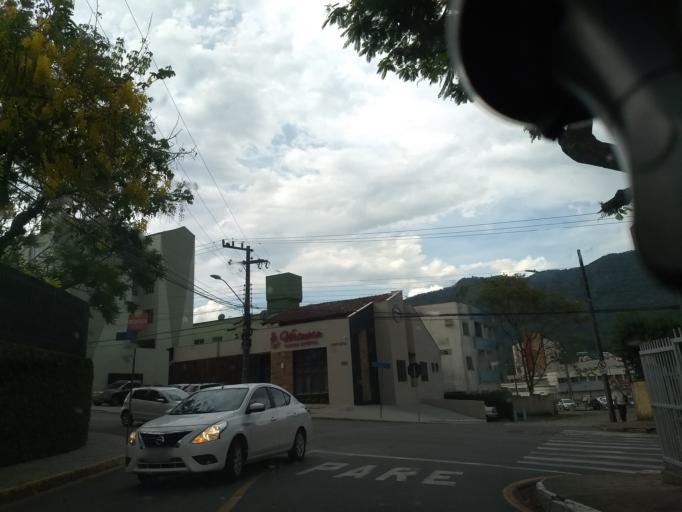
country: BR
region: Santa Catarina
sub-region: Jaragua Do Sul
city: Jaragua do Sul
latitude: -26.4800
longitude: -49.0880
